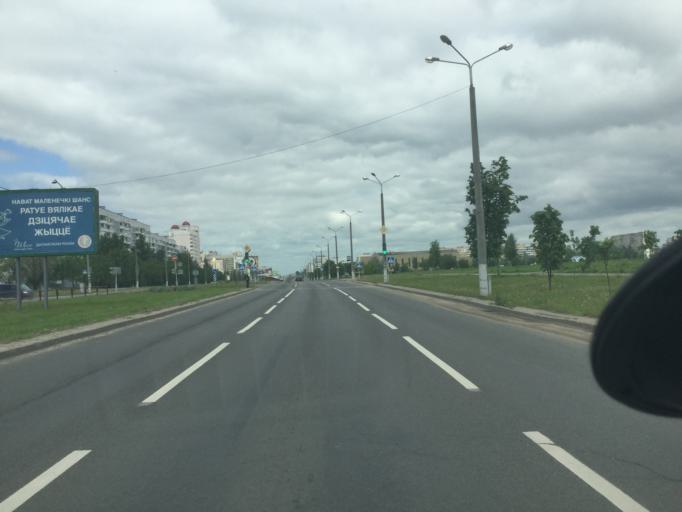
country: BY
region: Vitebsk
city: Vitebsk
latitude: 55.1641
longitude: 30.2231
